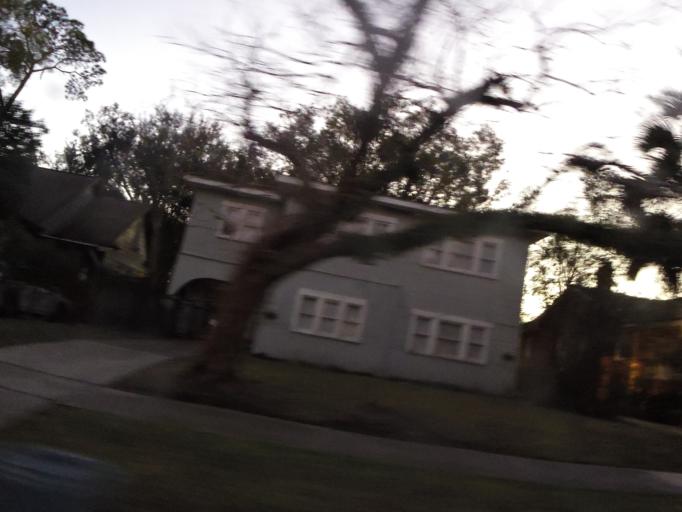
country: US
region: Florida
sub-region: Duval County
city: Jacksonville
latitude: 30.3023
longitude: -81.7103
